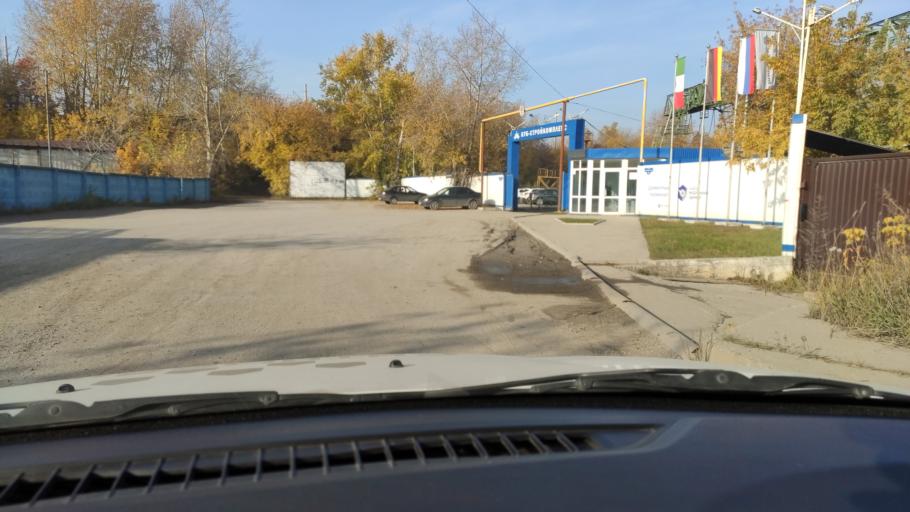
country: RU
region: Perm
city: Kondratovo
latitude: 58.0065
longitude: 56.1604
